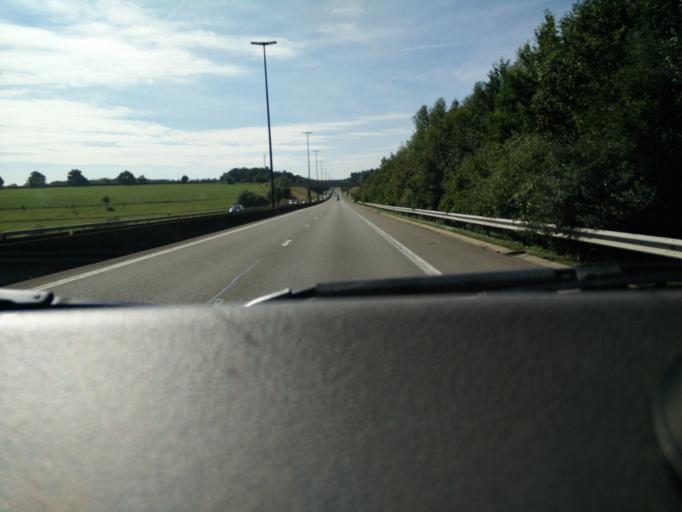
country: BE
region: Wallonia
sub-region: Province du Luxembourg
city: Libin
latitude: 49.9628
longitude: 5.2382
